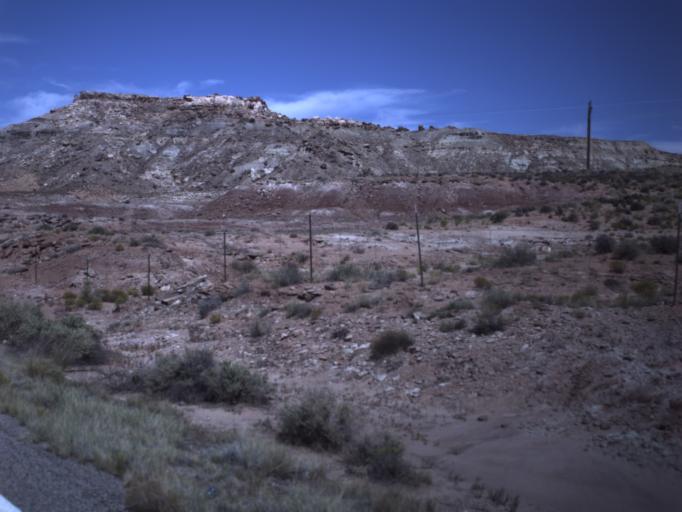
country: US
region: Utah
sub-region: San Juan County
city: Blanding
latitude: 37.2966
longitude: -109.4271
